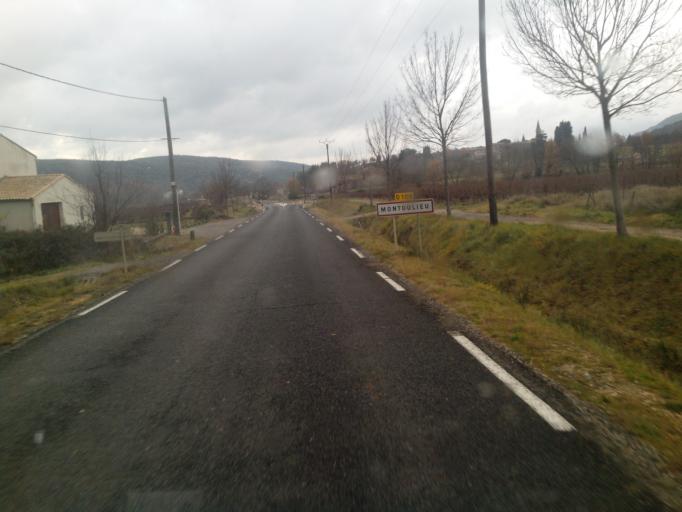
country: FR
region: Languedoc-Roussillon
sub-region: Departement du Gard
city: Saint-Hippolyte-du-Fort
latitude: 43.9302
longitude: 3.7956
